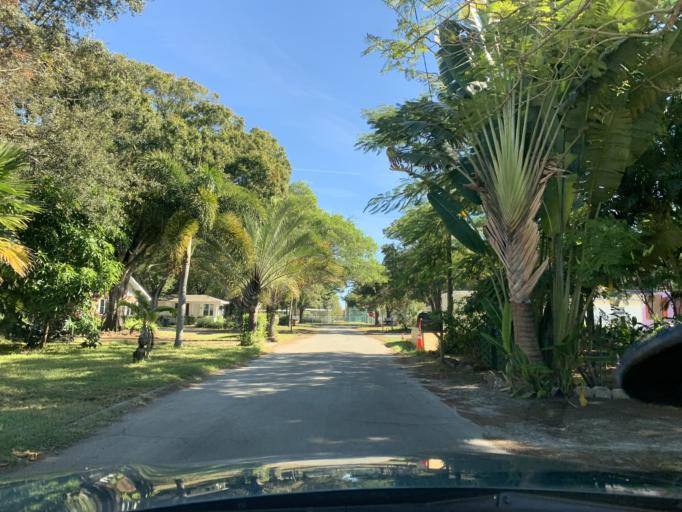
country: US
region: Florida
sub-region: Pinellas County
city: Gulfport
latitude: 27.7520
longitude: -82.7090
